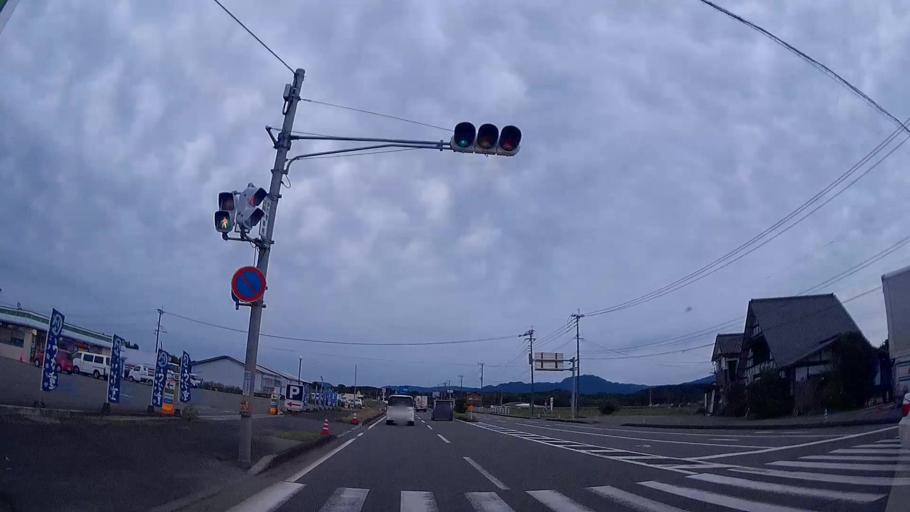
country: JP
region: Kumamoto
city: Kikuchi
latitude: 32.9321
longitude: 130.8305
